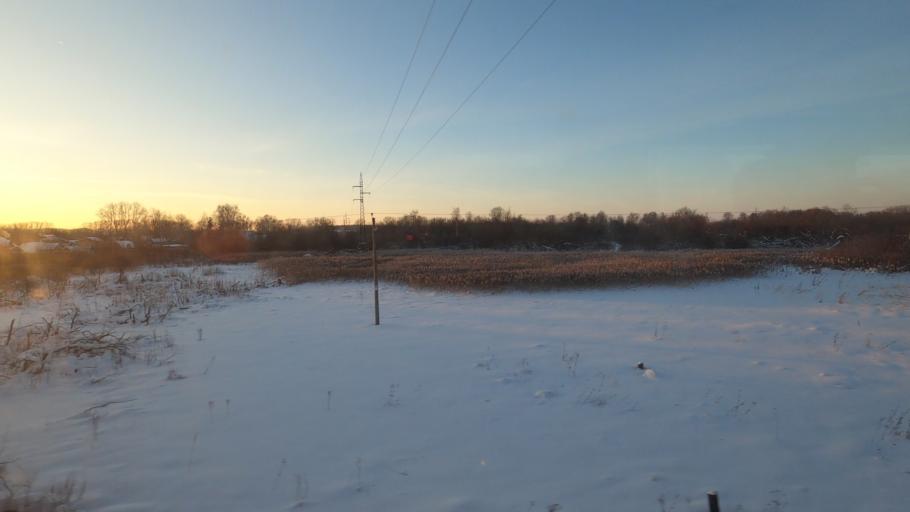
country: RU
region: Moskovskaya
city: Dmitrov
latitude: 56.3574
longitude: 37.5208
